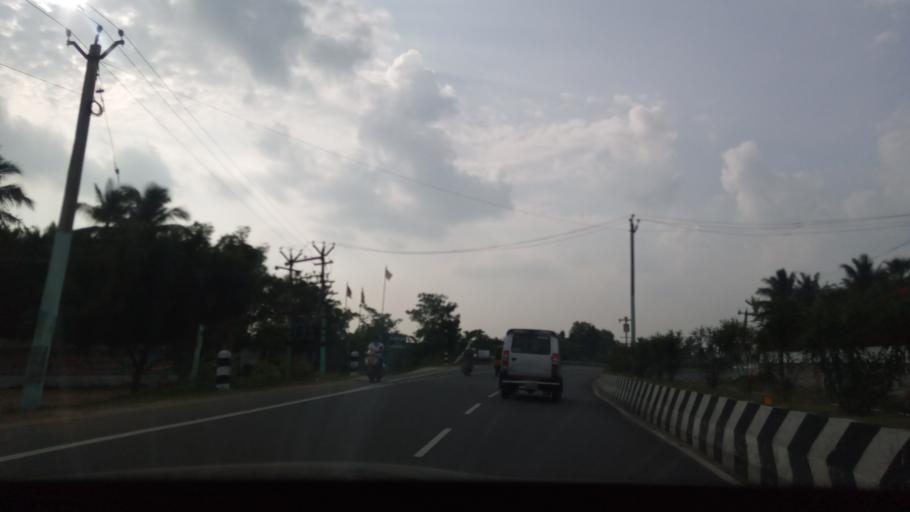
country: IN
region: Tamil Nadu
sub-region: Kancheepuram
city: Injambakkam
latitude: 12.7779
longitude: 80.2487
